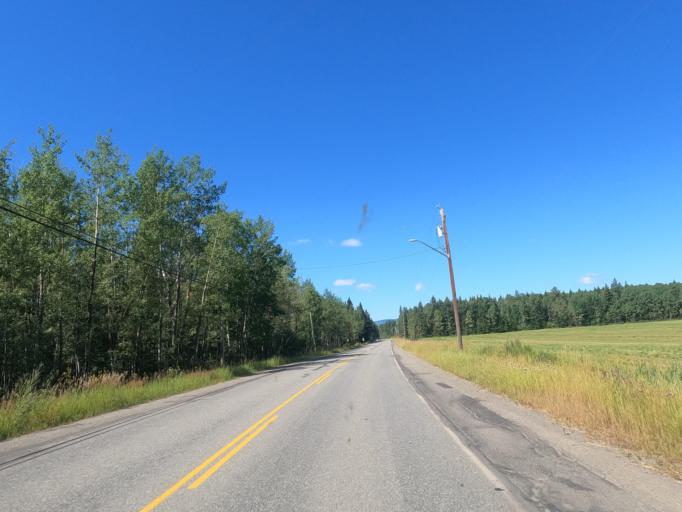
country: CA
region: British Columbia
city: Quesnel
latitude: 53.0196
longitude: -122.4621
